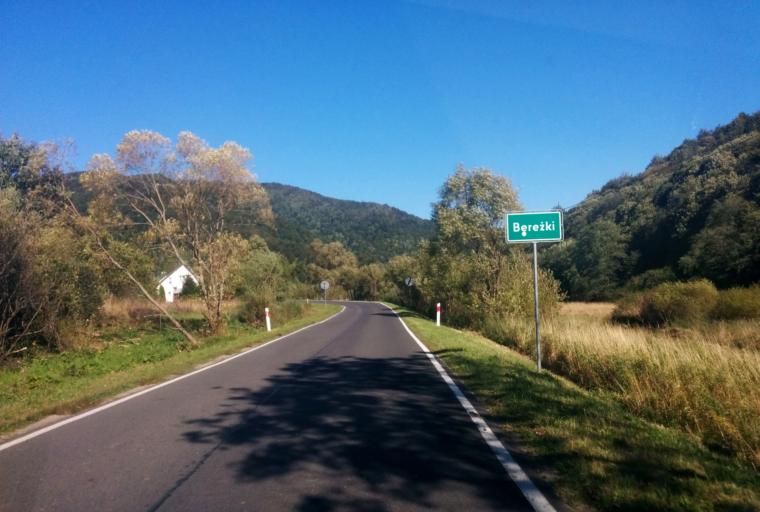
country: PL
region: Subcarpathian Voivodeship
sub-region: Powiat bieszczadzki
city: Lutowiska
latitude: 49.1345
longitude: 22.6693
